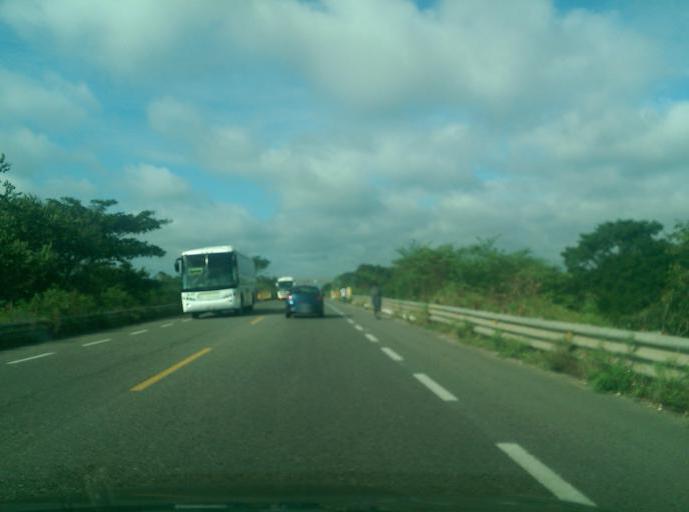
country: MX
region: Tabasco
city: Aquiles Serdan
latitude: 17.6956
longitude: -92.2933
